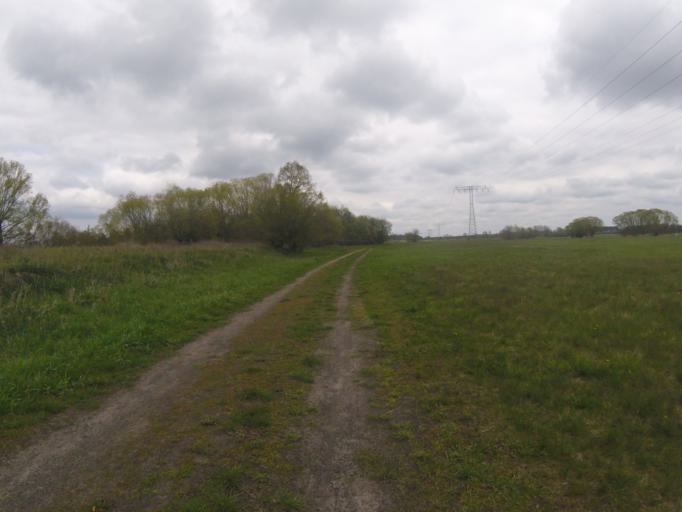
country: DE
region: Brandenburg
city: Mittenwalde
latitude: 52.2558
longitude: 13.5674
